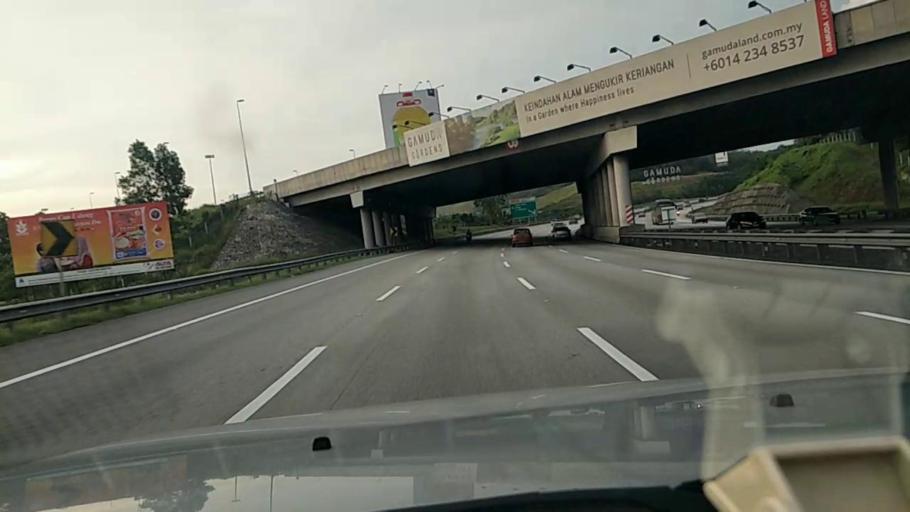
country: MY
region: Selangor
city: Kuang
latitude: 3.2653
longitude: 101.5517
